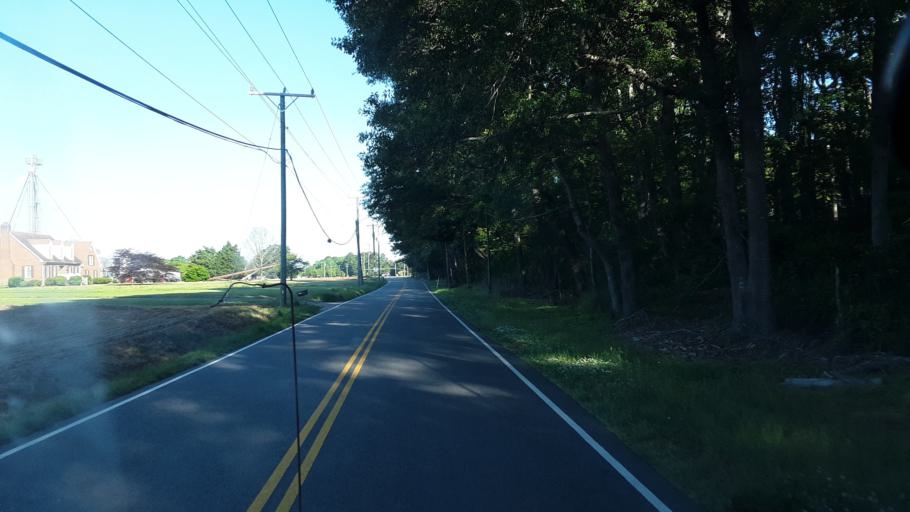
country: US
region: Virginia
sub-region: City of Virginia Beach
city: Virginia Beach
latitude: 36.7204
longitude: -76.0455
